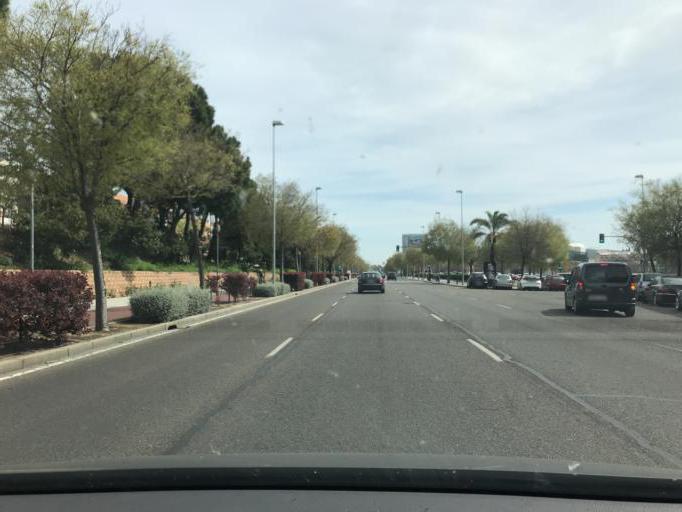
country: ES
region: Andalusia
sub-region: Province of Cordoba
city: Cordoba
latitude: 37.8932
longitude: -4.7790
